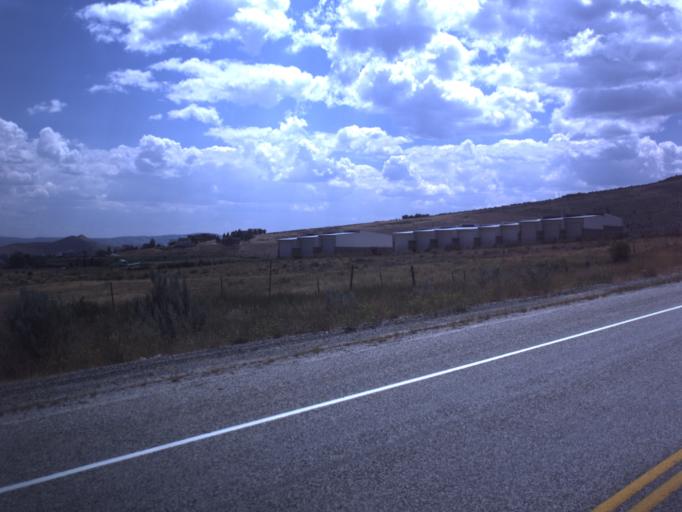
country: US
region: Idaho
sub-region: Bear Lake County
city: Paris
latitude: 41.9439
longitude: -111.4086
